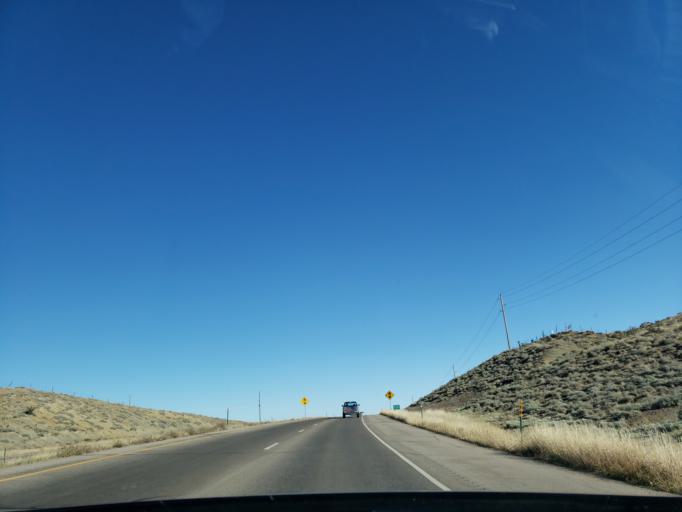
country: US
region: Colorado
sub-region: Fremont County
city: Lincoln Park
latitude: 38.4500
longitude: -105.1639
